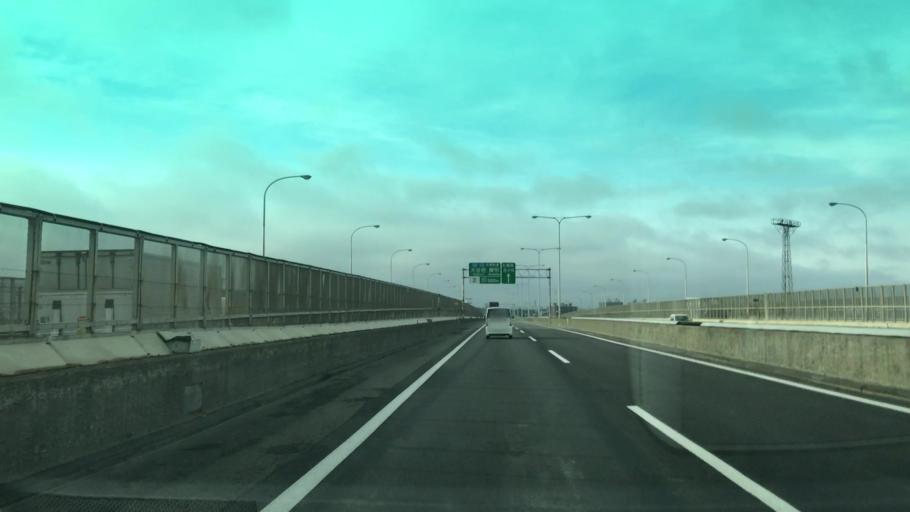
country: JP
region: Hokkaido
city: Sapporo
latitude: 43.0479
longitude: 141.4333
